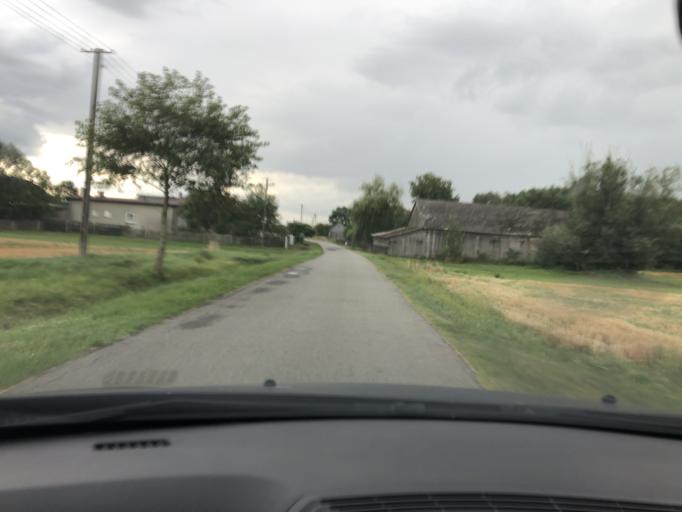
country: PL
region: Lodz Voivodeship
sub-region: Powiat wieruszowski
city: Czastary
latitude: 51.2421
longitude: 18.2805
